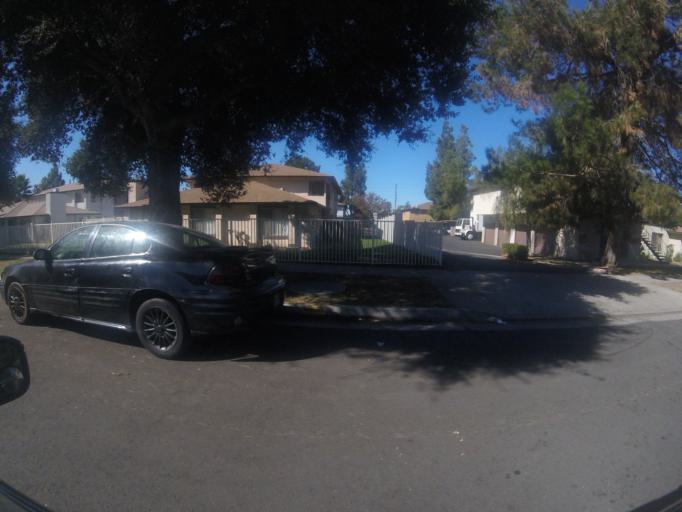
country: US
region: California
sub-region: San Bernardino County
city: Redlands
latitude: 34.0684
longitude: -117.1770
